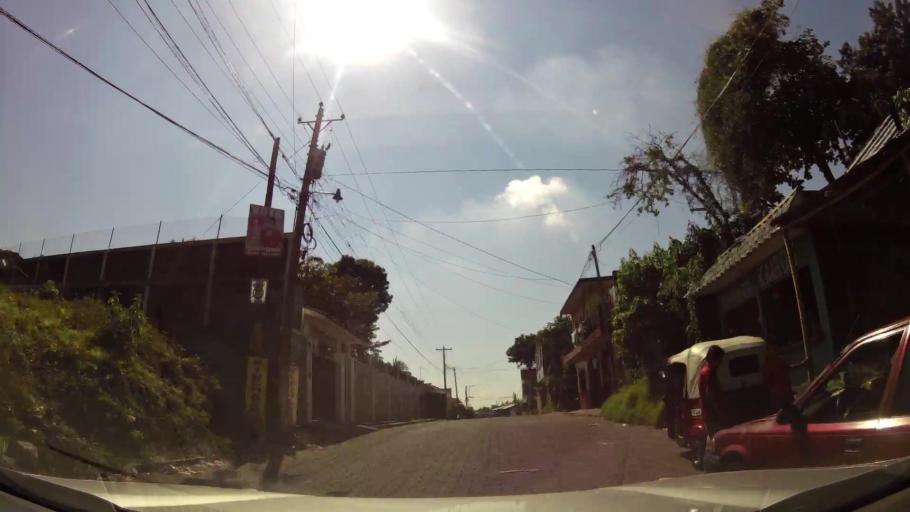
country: GT
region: Suchitepeque
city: Mazatenango
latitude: 14.5332
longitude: -91.4981
